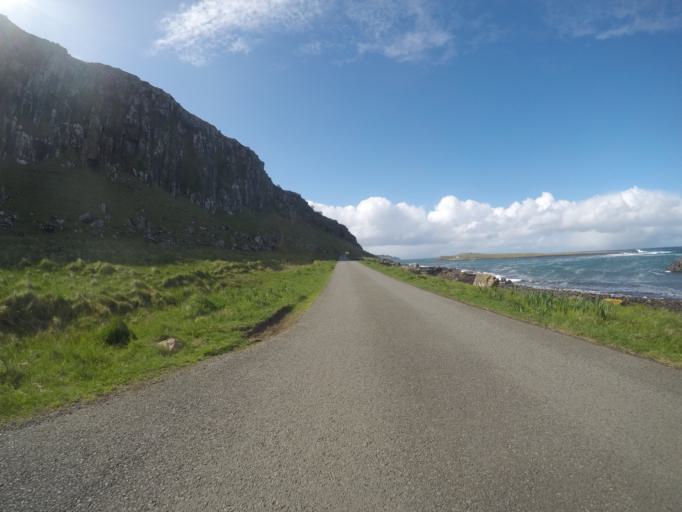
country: GB
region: Scotland
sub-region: Highland
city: Portree
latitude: 57.6333
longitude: -6.2002
